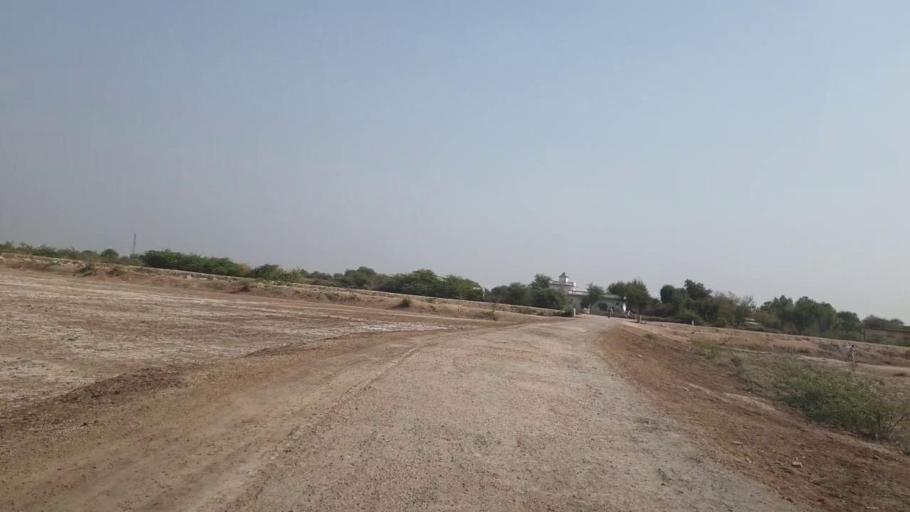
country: PK
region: Sindh
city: Dhoro Naro
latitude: 25.4825
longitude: 69.6556
